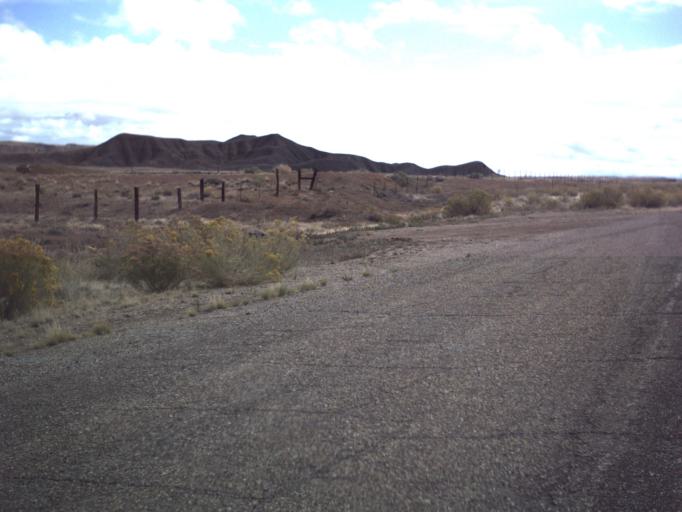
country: US
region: Utah
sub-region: Grand County
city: Moab
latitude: 38.9224
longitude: -109.9387
